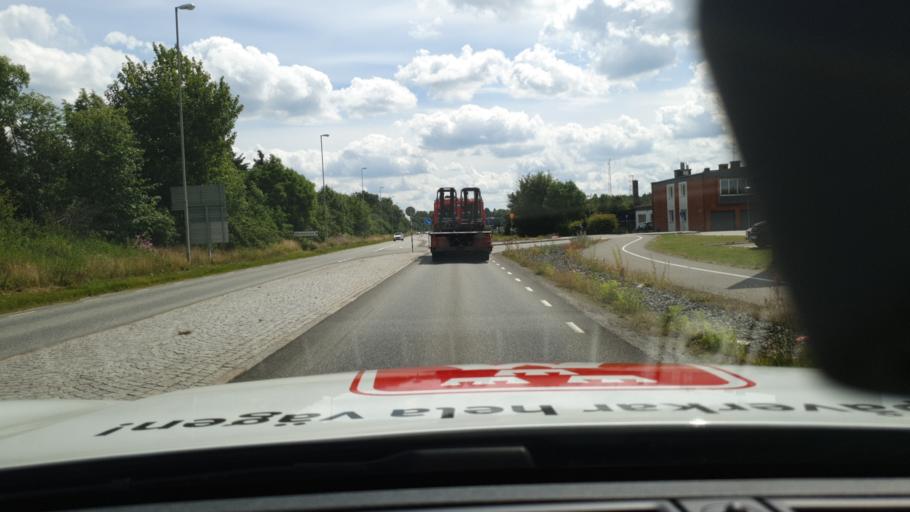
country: SE
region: Skane
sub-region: Hassleholms Kommun
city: Hassleholm
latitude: 56.1500
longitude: 13.7817
